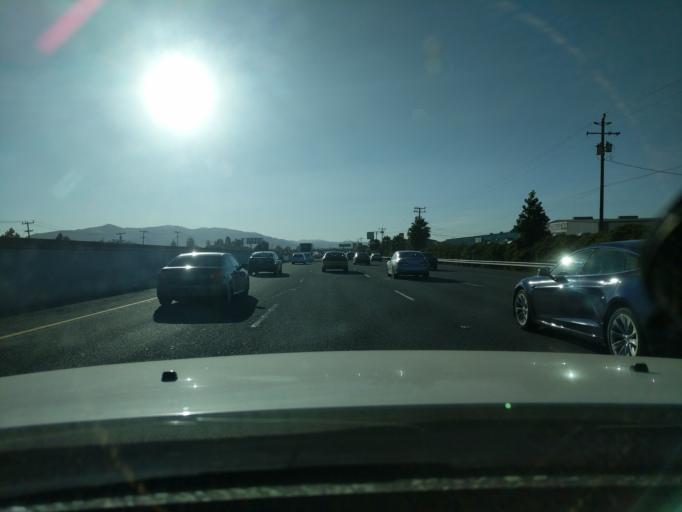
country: US
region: California
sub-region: Alameda County
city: Fremont
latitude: 37.5336
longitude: -122.0093
